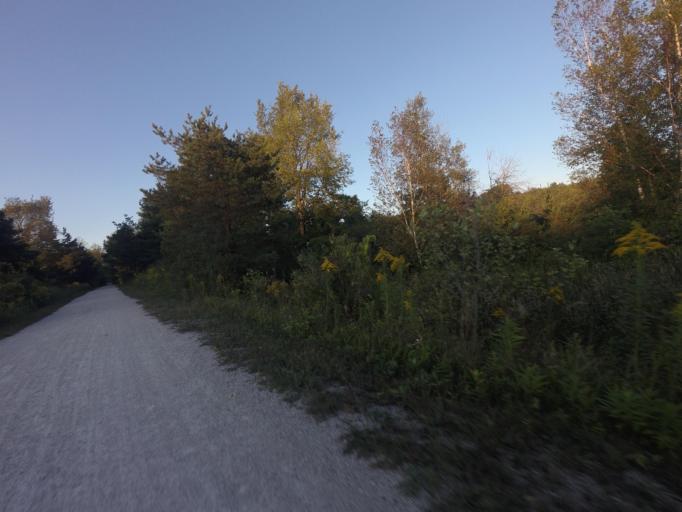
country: CA
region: Ontario
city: Brampton
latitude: 43.9061
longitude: -79.8390
